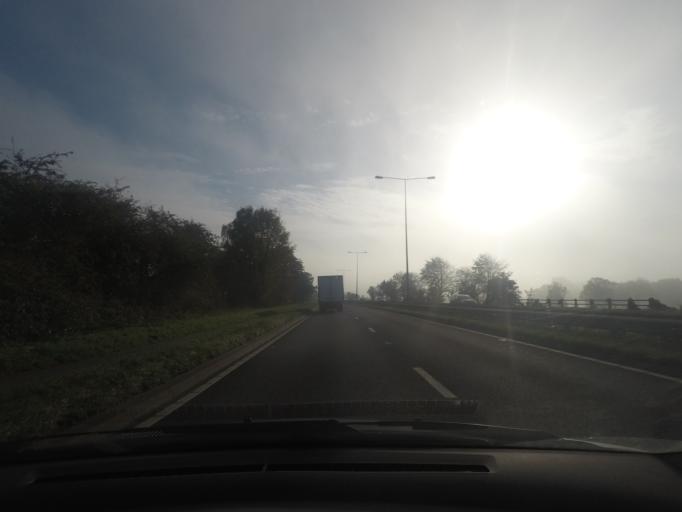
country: GB
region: England
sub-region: East Riding of Yorkshire
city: Welton
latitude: 53.7284
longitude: -0.5438
